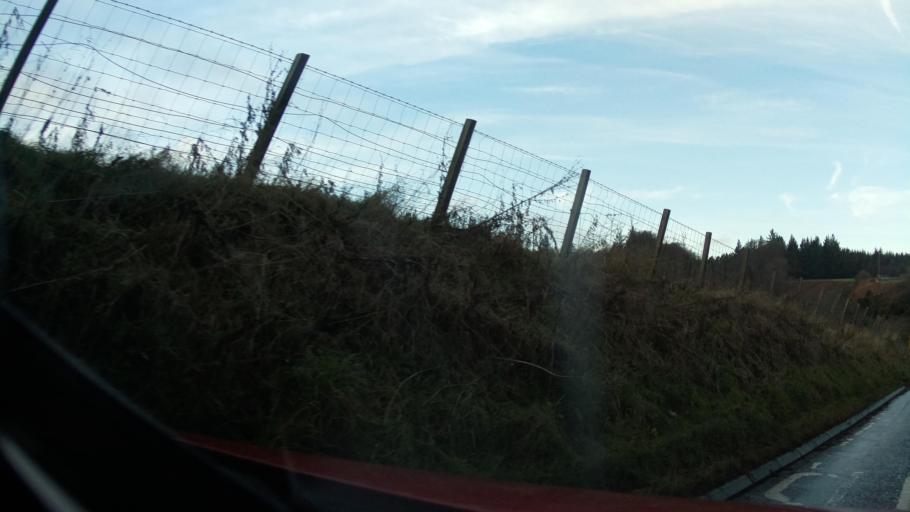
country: GB
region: Scotland
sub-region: Angus
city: Letham
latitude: 56.5506
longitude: -2.7640
